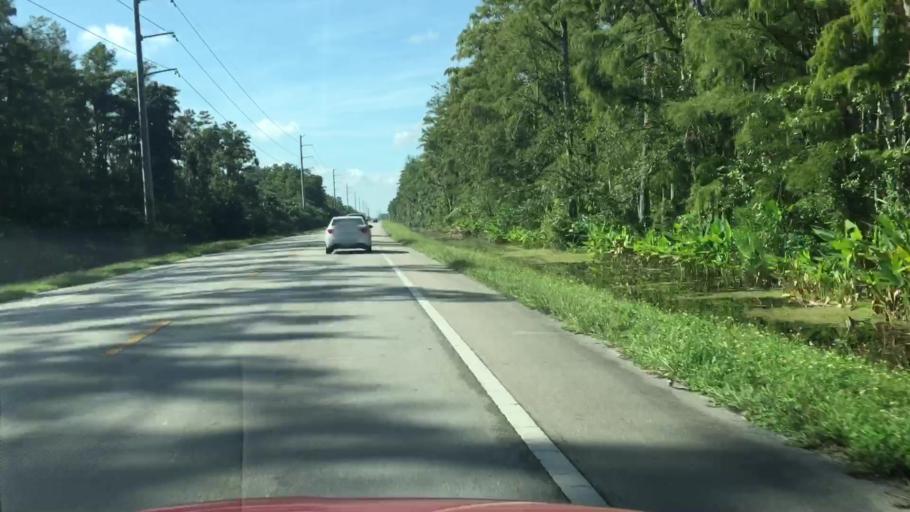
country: US
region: Florida
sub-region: Collier County
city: Orangetree
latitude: 26.3373
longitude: -81.5950
